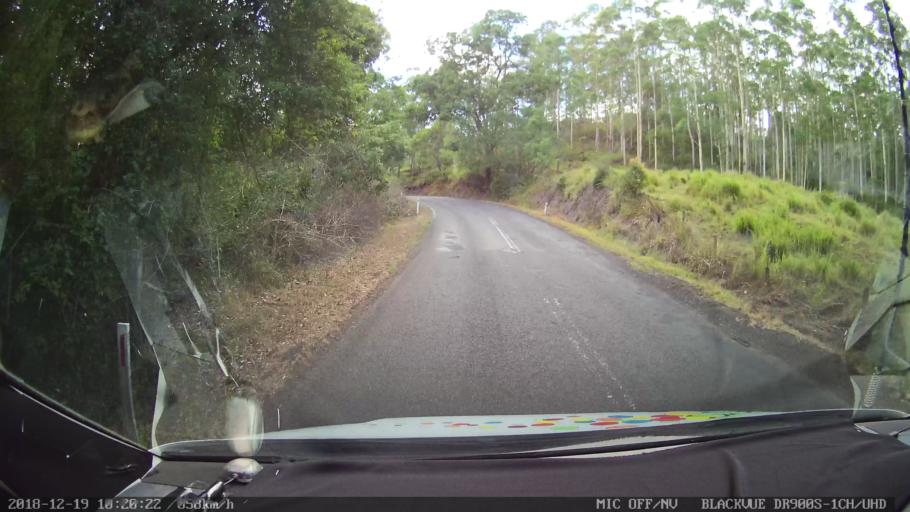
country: AU
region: New South Wales
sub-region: Kyogle
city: Kyogle
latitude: -28.6027
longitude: 153.0527
